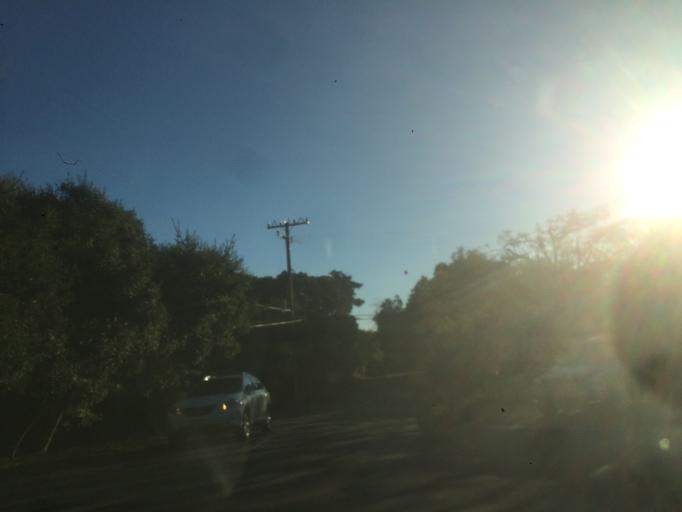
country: US
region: California
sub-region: Santa Barbara County
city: Goleta
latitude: 34.4200
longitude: -119.7725
